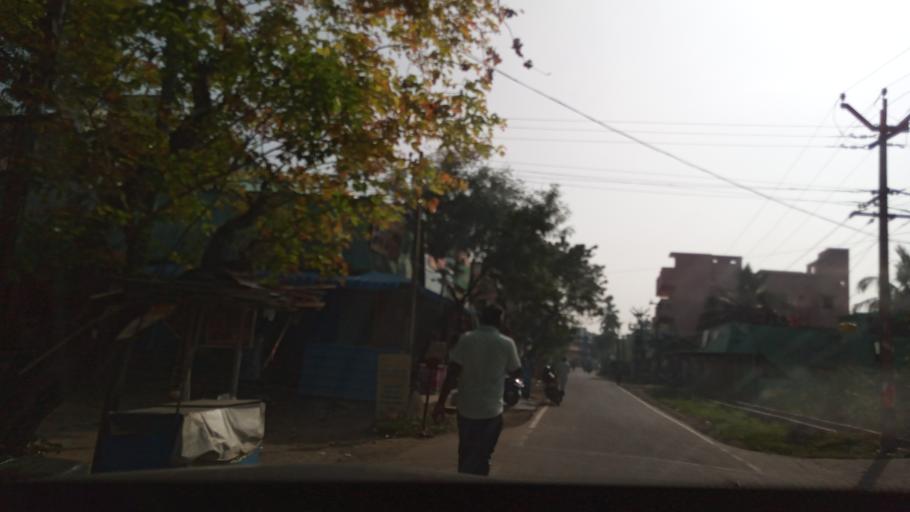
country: IN
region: Tamil Nadu
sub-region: Kancheepuram
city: Guduvancheri
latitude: 12.8519
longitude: 80.0687
